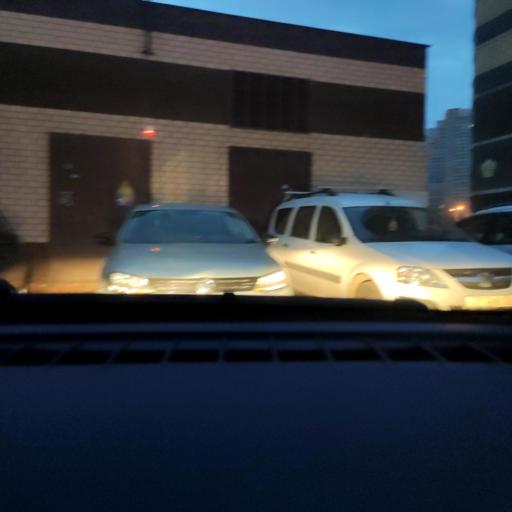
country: RU
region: Voronezj
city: Voronezh
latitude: 51.7133
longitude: 39.1964
